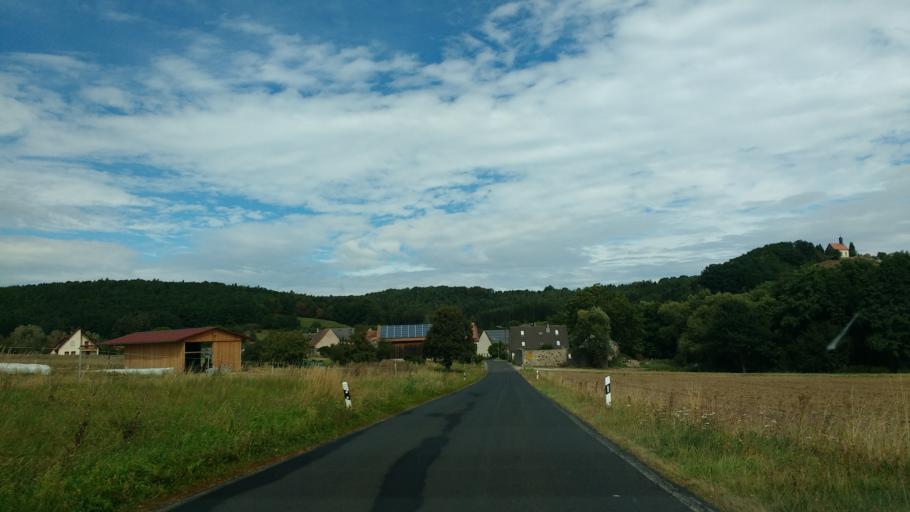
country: DE
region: Bavaria
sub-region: Regierungsbezirk Unterfranken
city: Geiselwind
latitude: 49.7703
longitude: 10.5338
